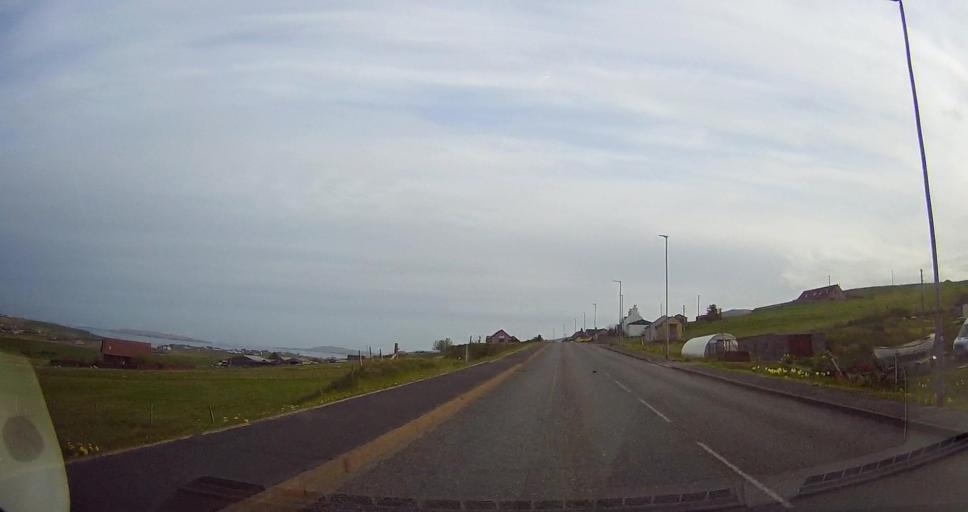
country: GB
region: Scotland
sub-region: Shetland Islands
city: Sandwick
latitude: 60.0515
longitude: -1.2265
